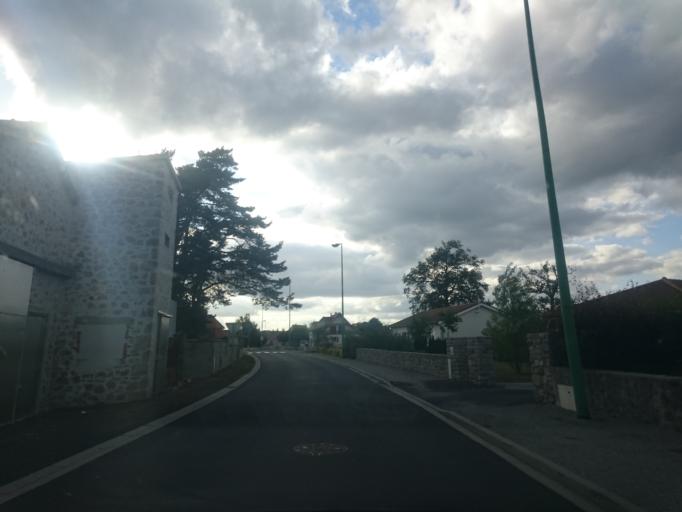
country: FR
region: Auvergne
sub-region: Departement du Cantal
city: Saint-Mamet-la-Salvetat
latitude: 44.8561
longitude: 2.2303
